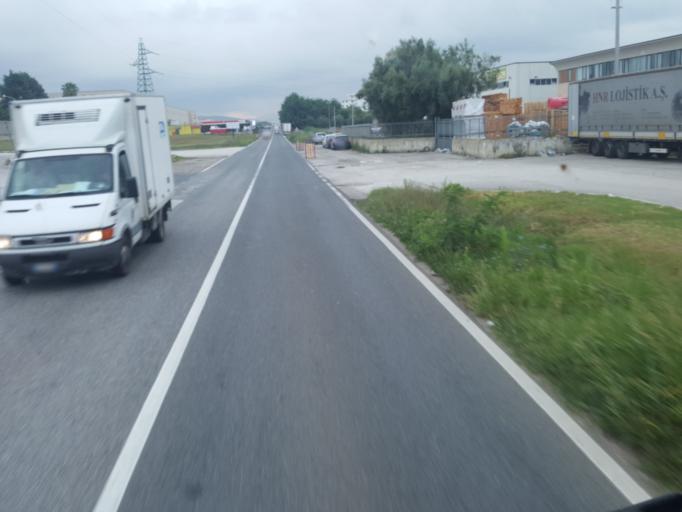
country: IT
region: Campania
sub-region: Provincia di Caserta
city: Pignataro Maggiore
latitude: 41.1656
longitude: 14.1602
